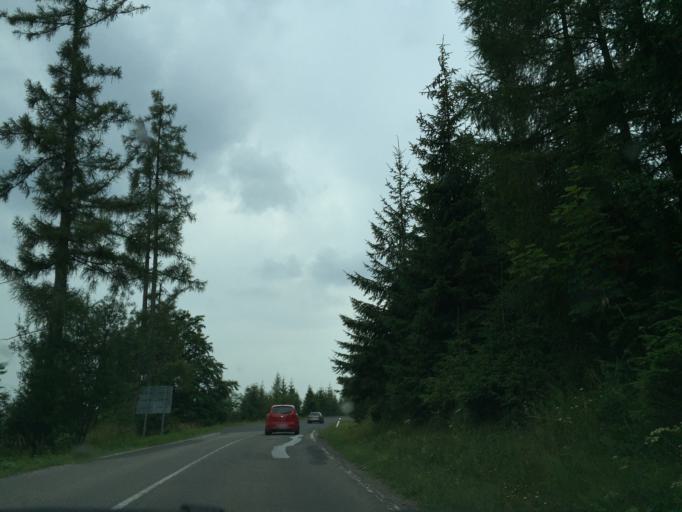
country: SK
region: Presovsky
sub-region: Okres Poprad
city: Vysoke Tatry
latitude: 49.1335
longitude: 20.2072
